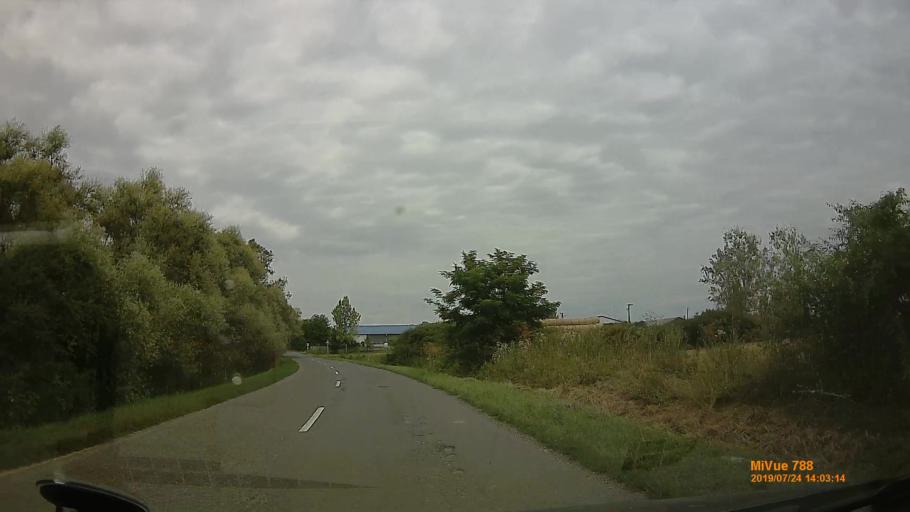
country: HU
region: Szabolcs-Szatmar-Bereg
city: Aranyosapati
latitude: 48.2765
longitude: 22.2863
